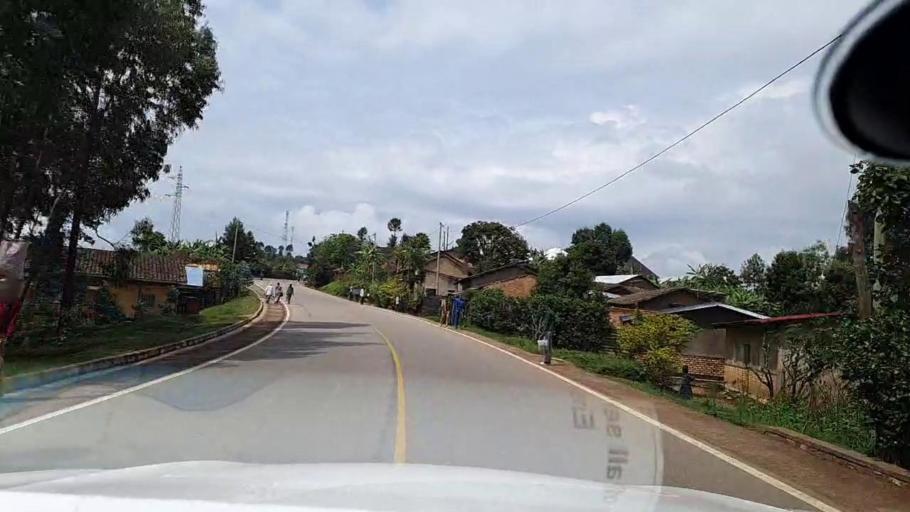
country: RW
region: Southern Province
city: Nzega
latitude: -2.4818
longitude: 29.5353
